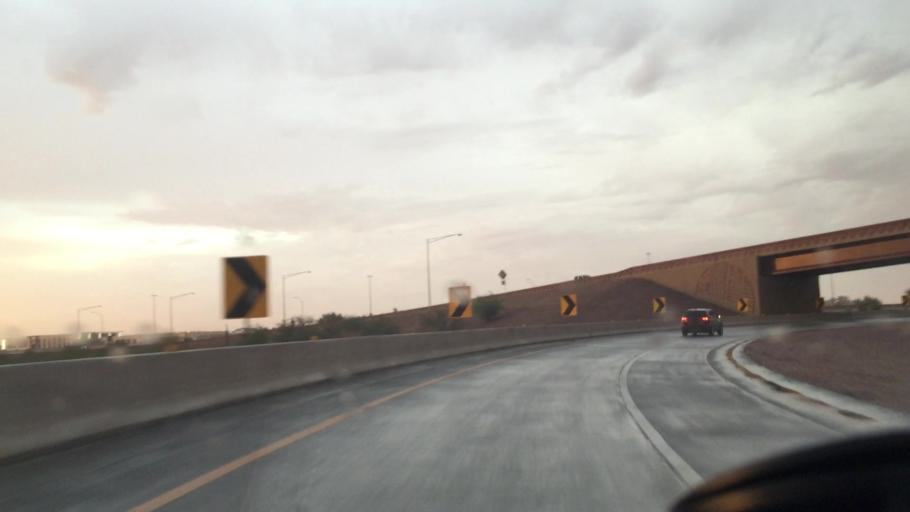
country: US
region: Arizona
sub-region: Maricopa County
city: Tempe Junction
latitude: 33.4389
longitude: -111.9760
